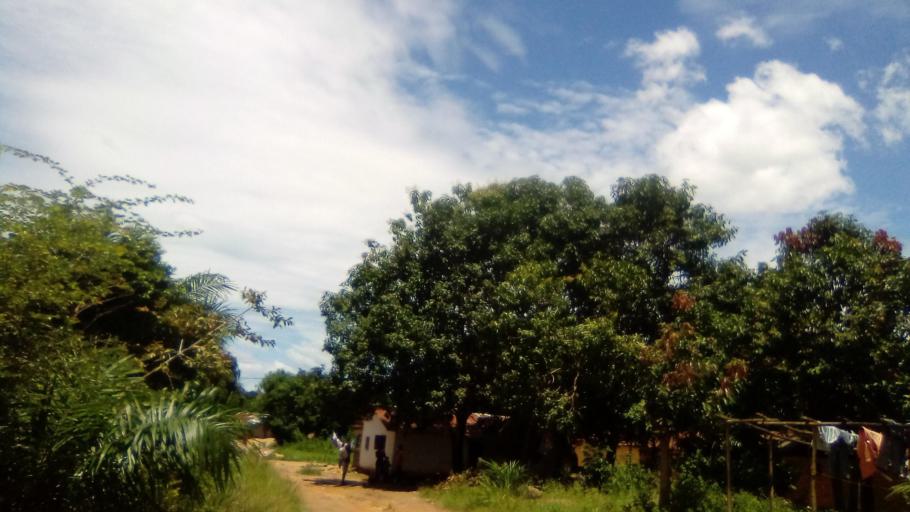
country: SL
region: Eastern Province
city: Simbakoro
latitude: 8.6259
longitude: -10.9879
